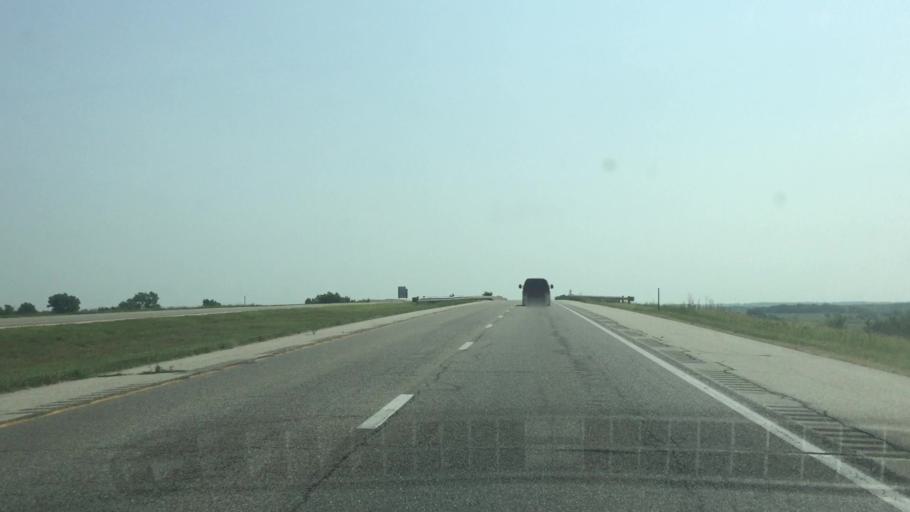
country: US
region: Kansas
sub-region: Osage County
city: Osage City
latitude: 38.4259
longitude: -95.8356
